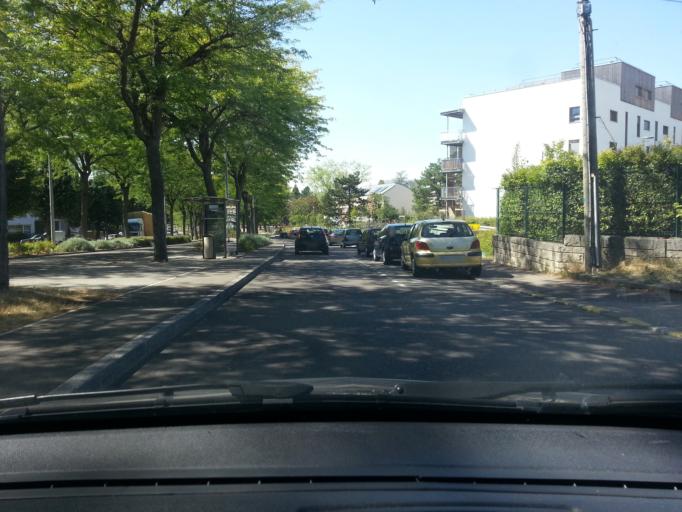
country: FR
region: Bourgogne
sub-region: Departement de la Cote-d'Or
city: Saint-Apollinaire
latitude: 47.3344
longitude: 5.0667
